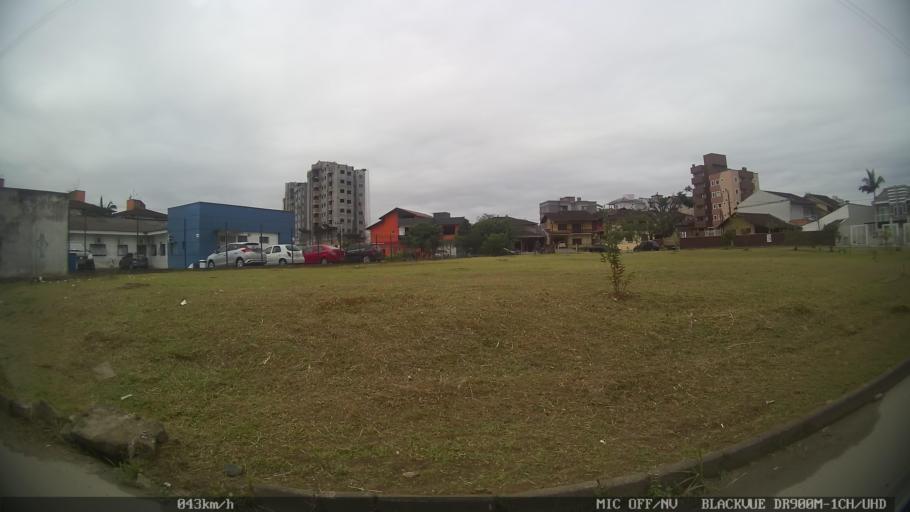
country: BR
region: Santa Catarina
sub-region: Joinville
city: Joinville
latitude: -26.2694
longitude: -48.8910
